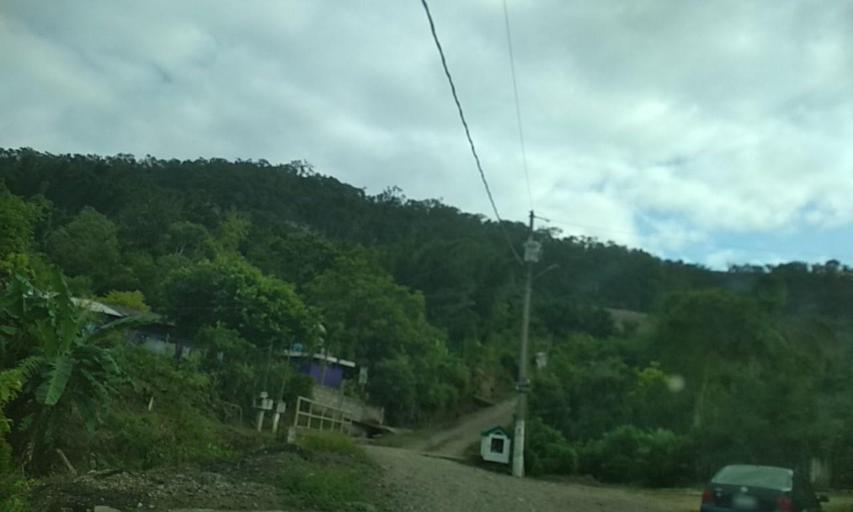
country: MX
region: Veracruz
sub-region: Papantla
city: Polutla
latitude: 20.5732
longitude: -97.2524
